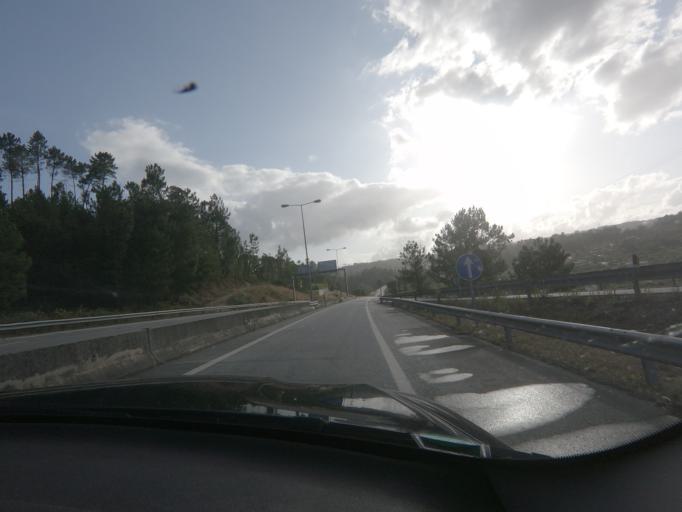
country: PT
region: Viseu
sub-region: Viseu
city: Viseu
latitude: 40.6030
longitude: -7.9780
